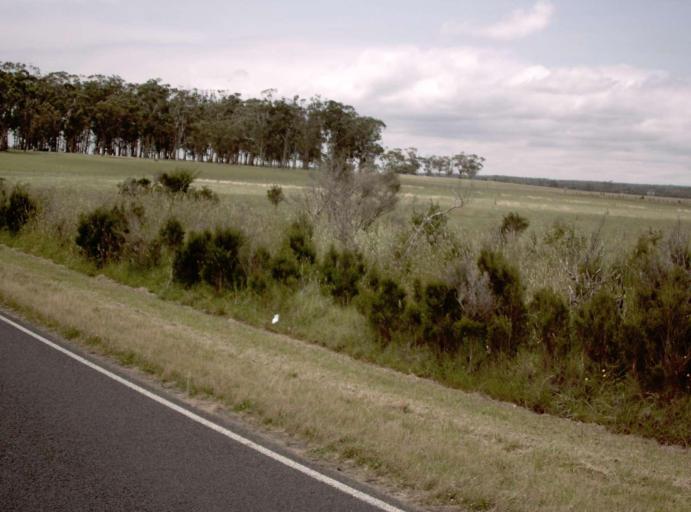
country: AU
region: Victoria
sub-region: Latrobe
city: Traralgon
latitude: -38.5452
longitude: 146.6557
